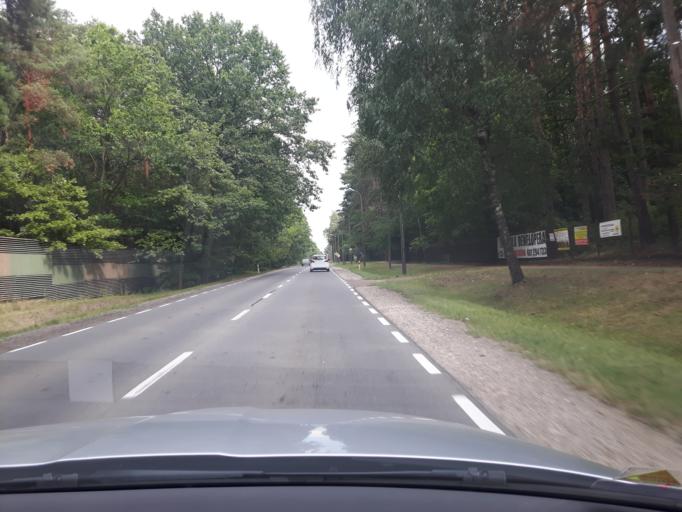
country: PL
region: Masovian Voivodeship
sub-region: Powiat piaseczynski
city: Lesznowola
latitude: 52.0992
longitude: 20.9025
